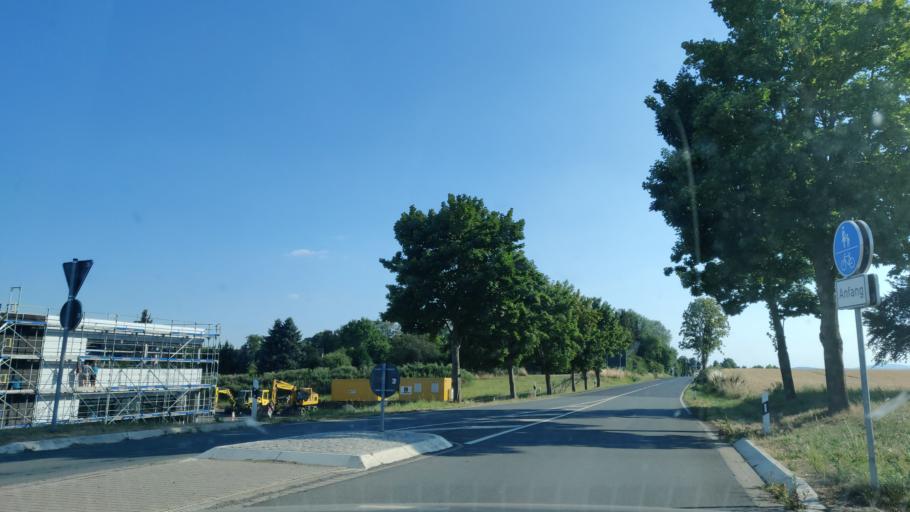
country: DE
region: Hesse
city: Gudensberg
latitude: 51.1798
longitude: 9.3583
